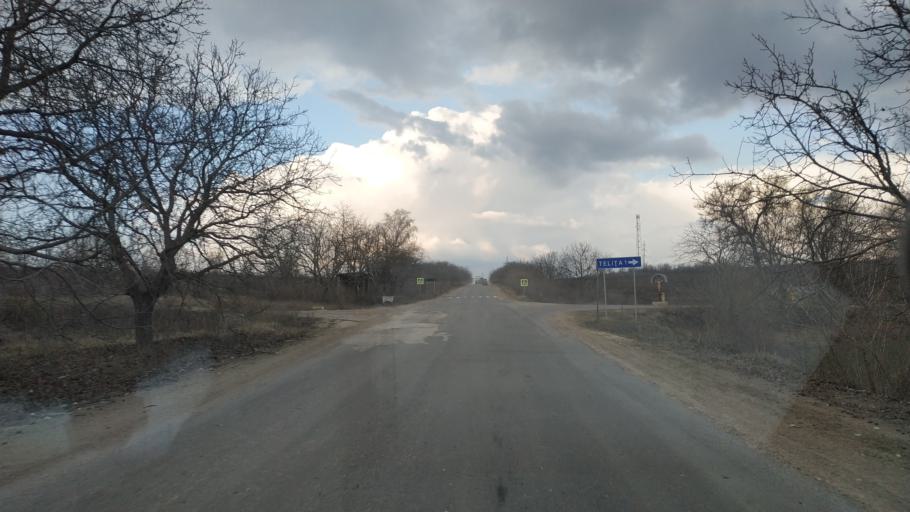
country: MD
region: Anenii Noi
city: Anenii Noi
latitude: 46.9569
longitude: 29.2834
